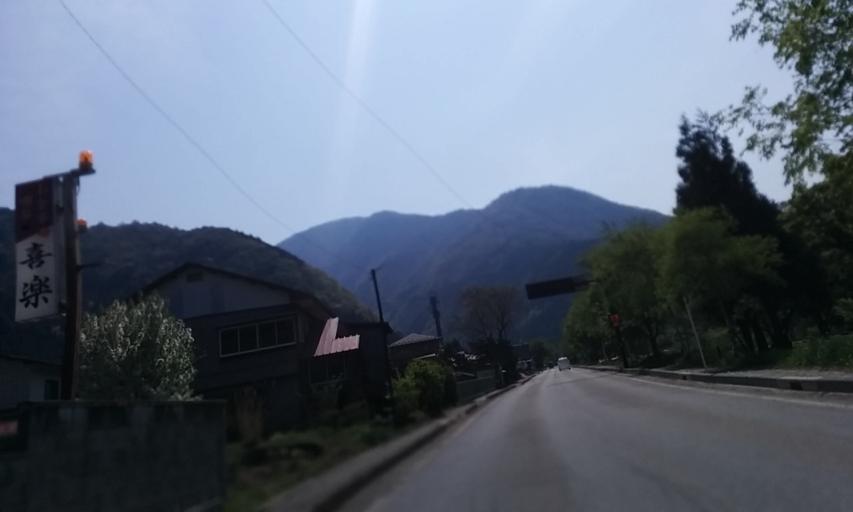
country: JP
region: Gifu
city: Takayama
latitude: 36.2473
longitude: 137.5196
